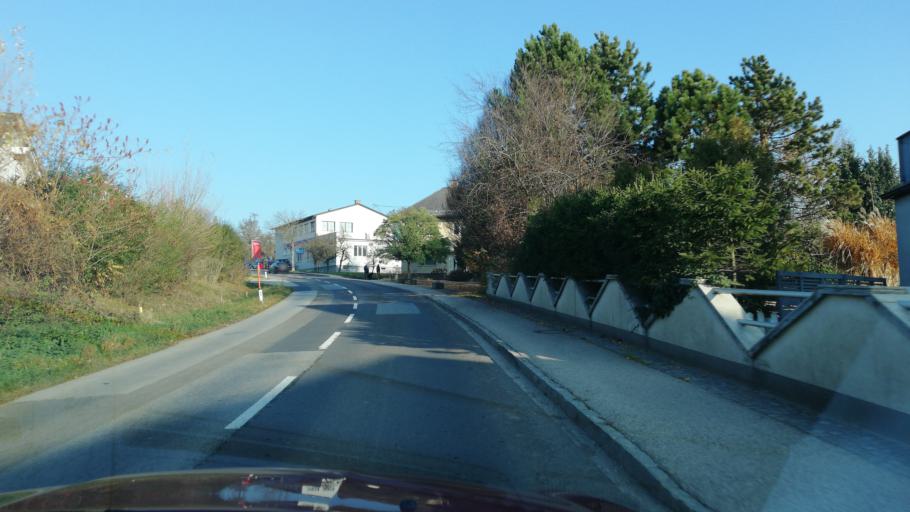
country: AT
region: Upper Austria
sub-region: Wels-Land
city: Buchkirchen
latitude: 48.2347
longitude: 14.0273
